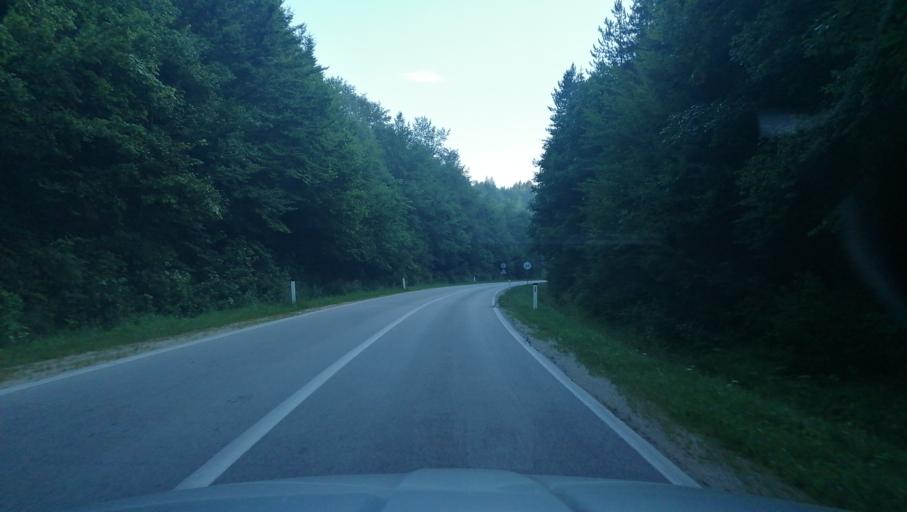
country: BA
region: Federation of Bosnia and Herzegovina
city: Prozor
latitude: 43.8762
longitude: 17.5921
